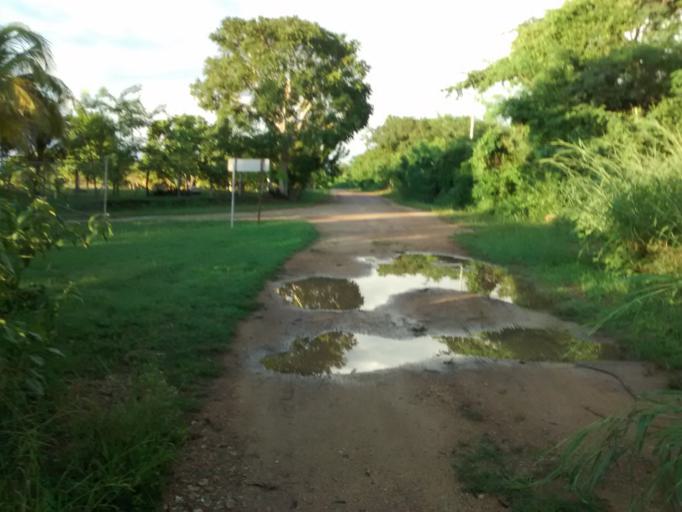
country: MX
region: Yucatan
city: Valladolid
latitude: 20.7218
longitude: -88.2057
